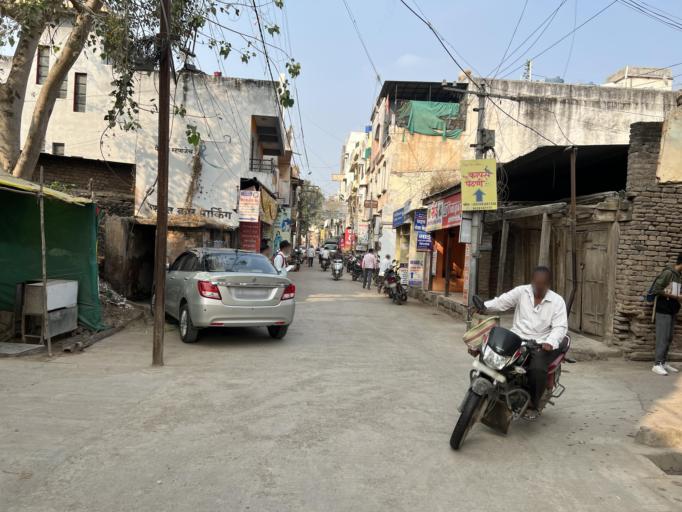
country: IN
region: Maharashtra
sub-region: Nashik Division
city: Yeola
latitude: 20.0403
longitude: 74.4900
